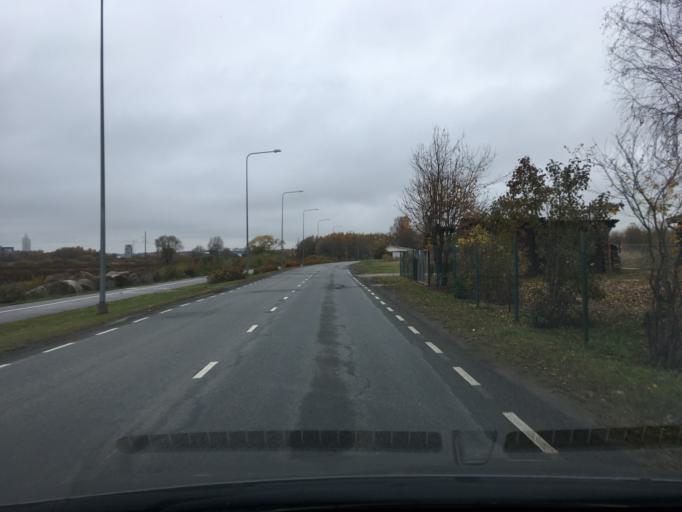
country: EE
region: Tartu
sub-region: Tartu linn
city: Tartu
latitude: 58.3623
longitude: 26.7594
